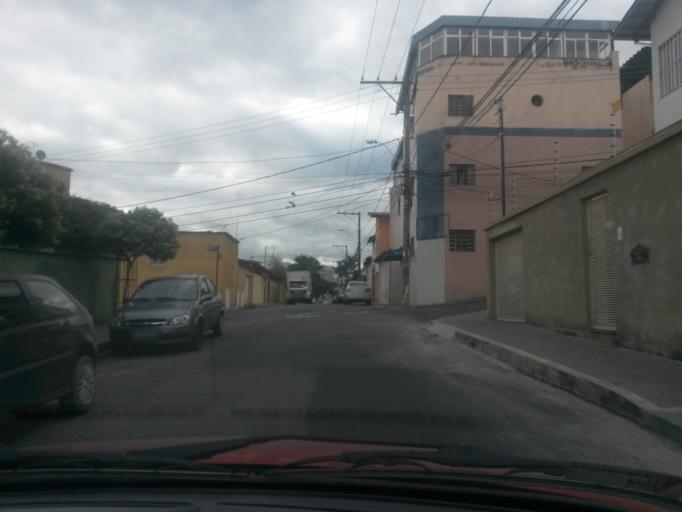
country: BR
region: Minas Gerais
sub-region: Belo Horizonte
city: Belo Horizonte
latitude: -19.9115
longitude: -43.9732
